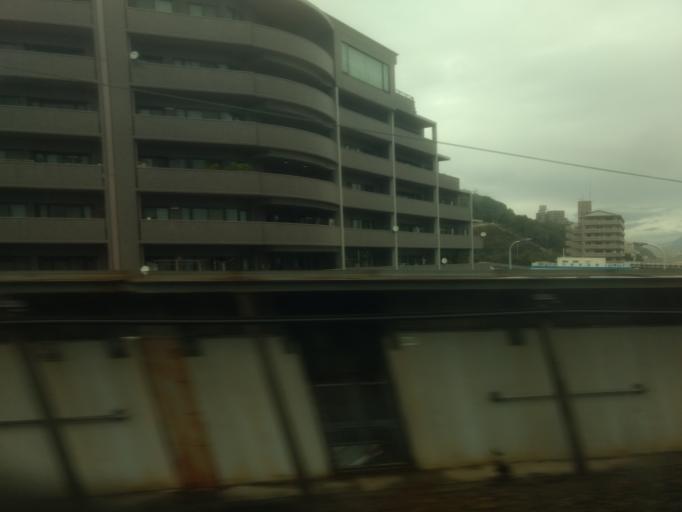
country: JP
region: Hiroshima
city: Hiroshima-shi
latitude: 34.4092
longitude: 132.4415
